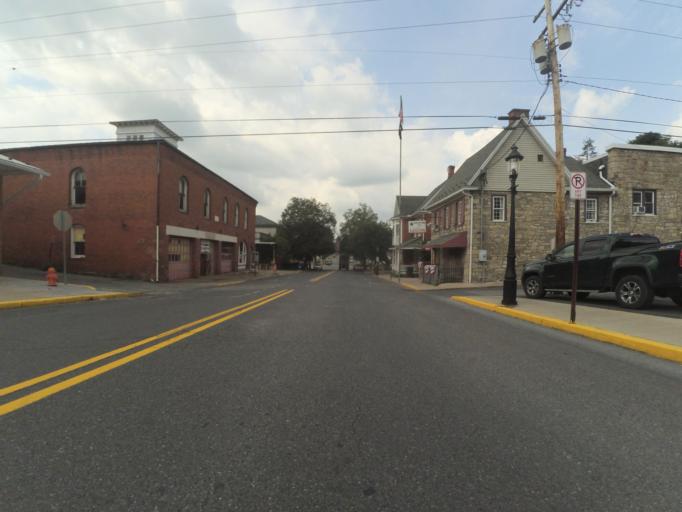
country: US
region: Pennsylvania
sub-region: Centre County
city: Bellefonte
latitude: 40.9136
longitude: -77.7774
